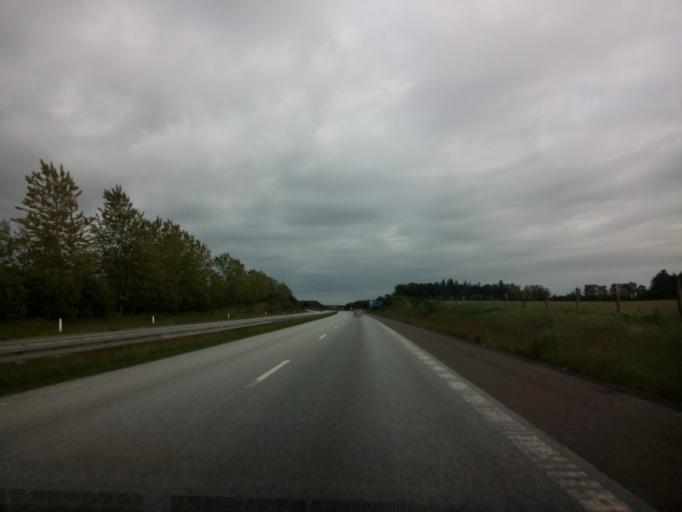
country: DK
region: North Denmark
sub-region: Hjorring Kommune
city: Vra
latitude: 57.3686
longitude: 10.0235
